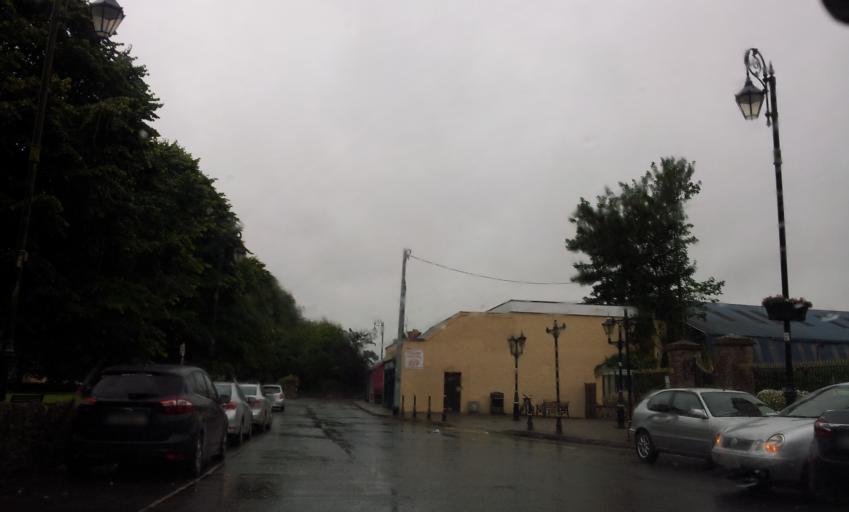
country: IE
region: Munster
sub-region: County Cork
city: Blarney
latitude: 51.9330
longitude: -8.5679
